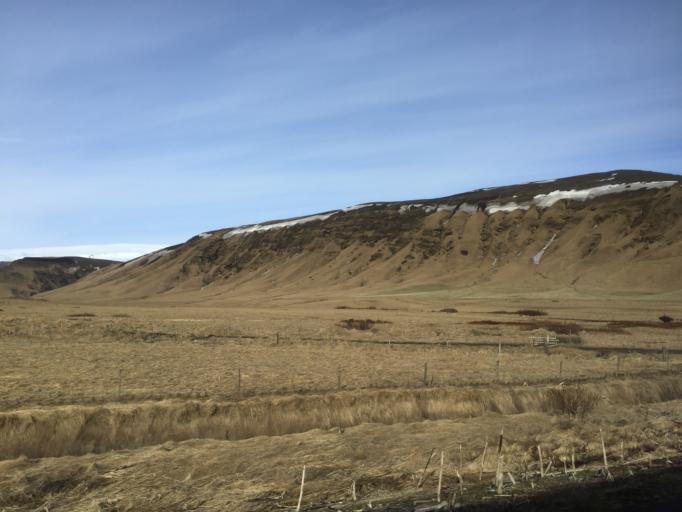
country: IS
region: South
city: Vestmannaeyjar
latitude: 63.4472
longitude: -19.1328
